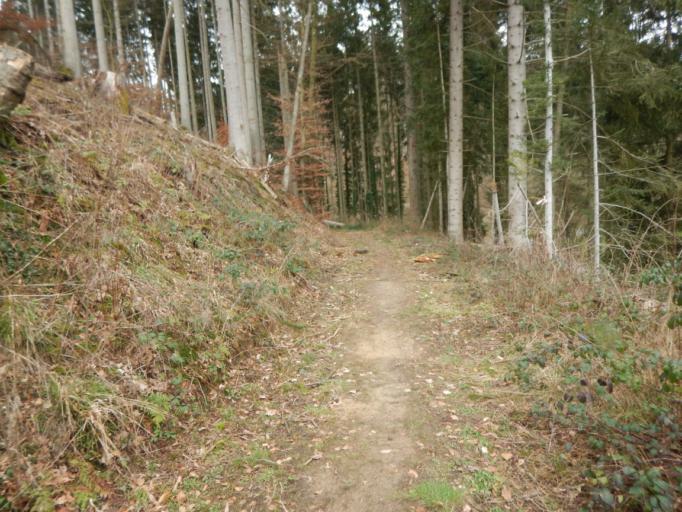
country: LU
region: Luxembourg
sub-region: Canton de Mersch
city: Tuntange
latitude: 49.7123
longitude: 6.0558
